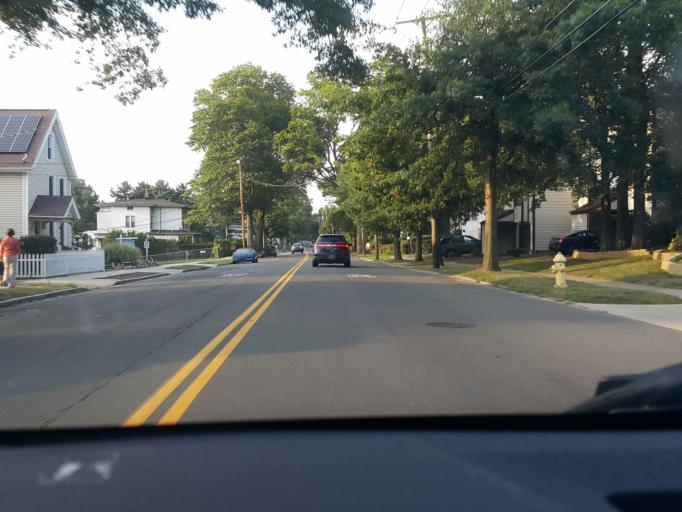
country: US
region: Connecticut
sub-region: New Haven County
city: East Haven
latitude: 41.2827
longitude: -72.8969
